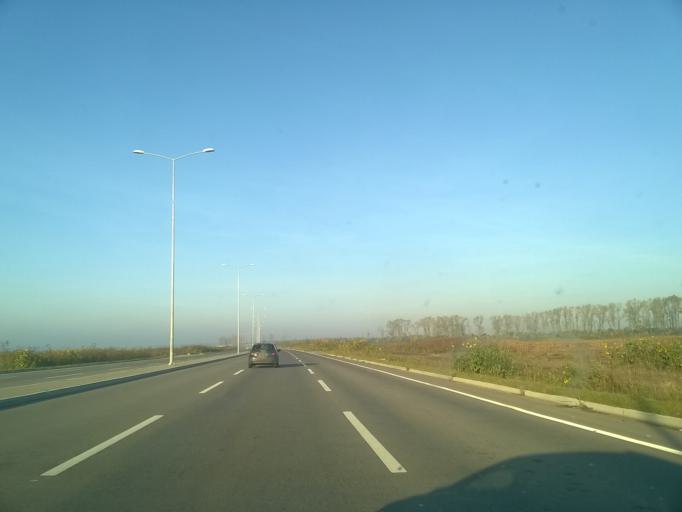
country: RS
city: Ovca
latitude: 44.9134
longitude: 20.4932
